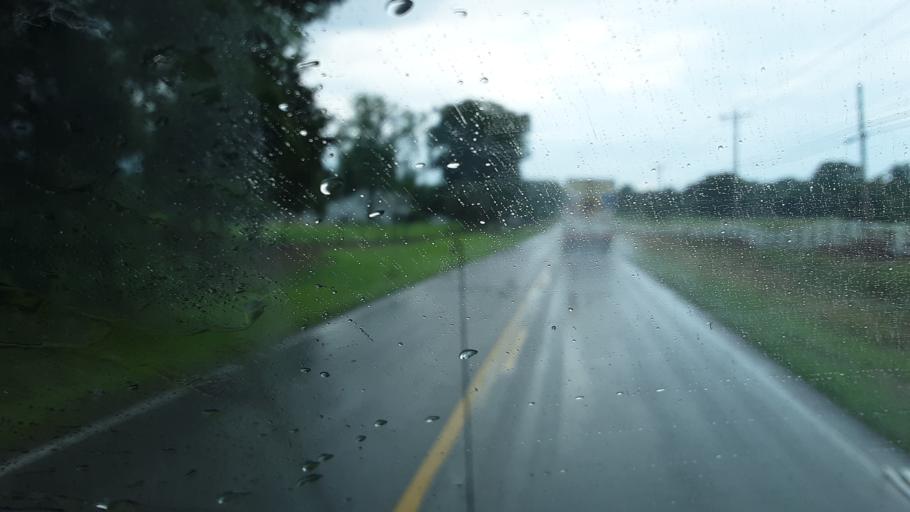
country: US
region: Kentucky
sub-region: Logan County
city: Russellville
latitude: 36.8246
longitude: -86.9140
